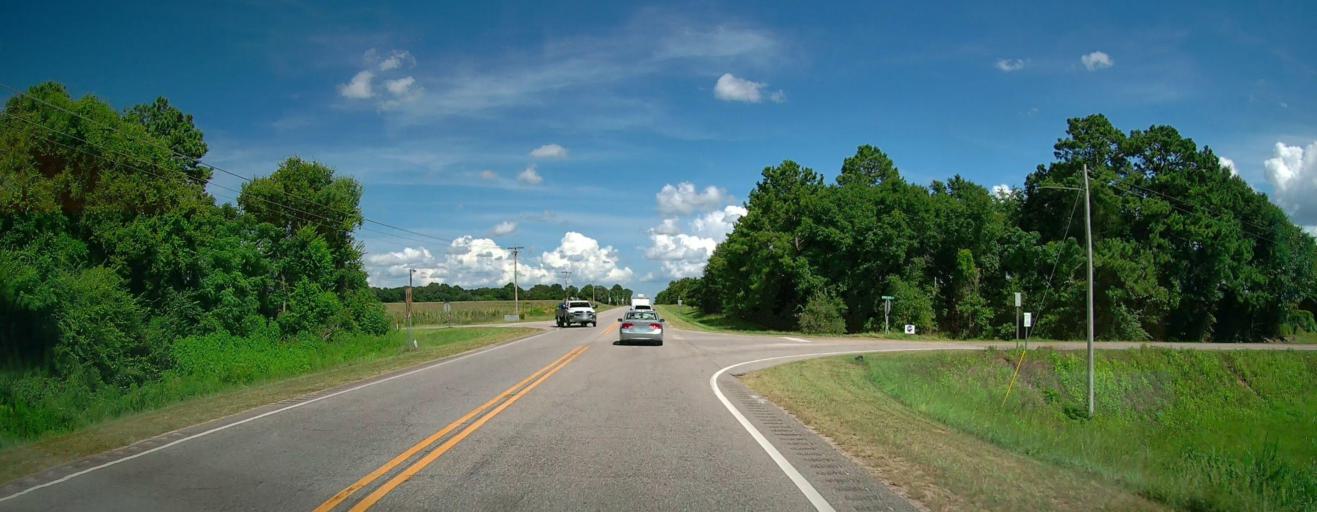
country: US
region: Alabama
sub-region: Elmore County
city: Tallassee
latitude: 32.3955
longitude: -85.9080
